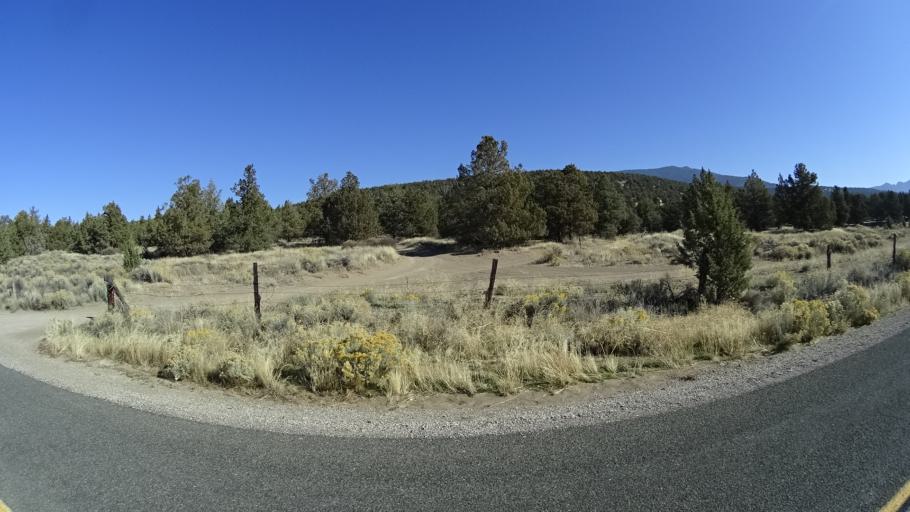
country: US
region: California
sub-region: Siskiyou County
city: Weed
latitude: 41.6207
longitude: -122.3232
